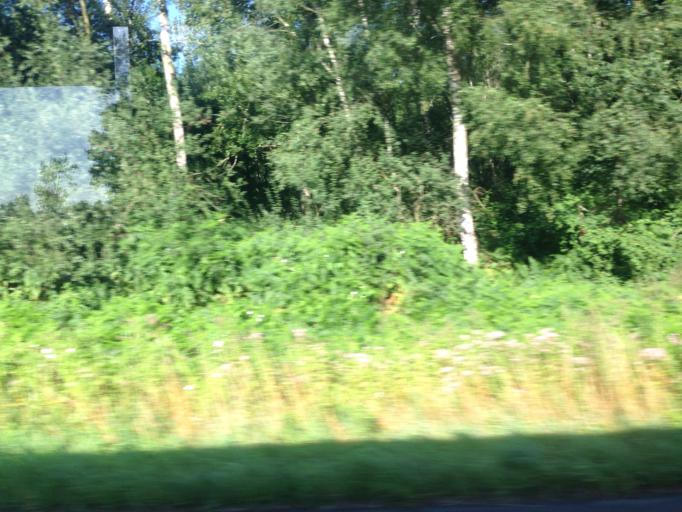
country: DE
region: North Rhine-Westphalia
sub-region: Regierungsbezirk Munster
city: Senden
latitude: 51.8832
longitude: 7.4975
